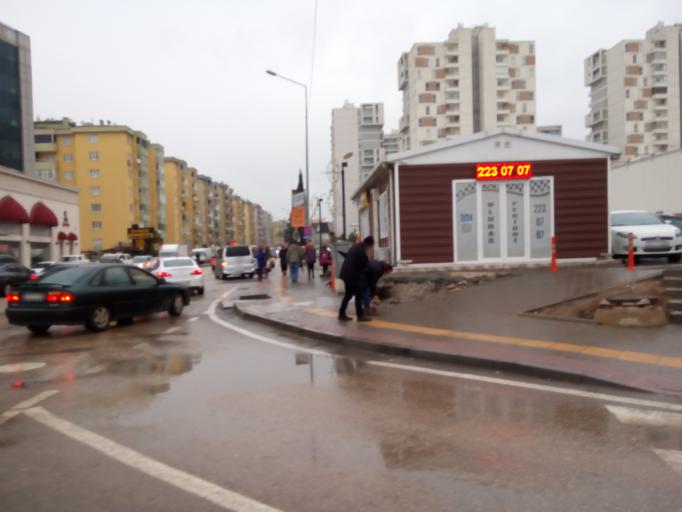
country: TR
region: Bursa
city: Niluefer
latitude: 40.2517
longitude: 28.9565
